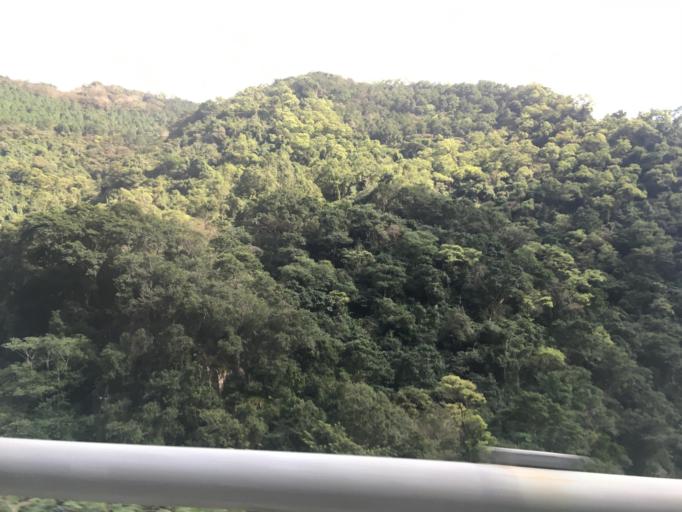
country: TW
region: Taiwan
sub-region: Yilan
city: Yilan
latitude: 24.7535
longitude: 121.6629
